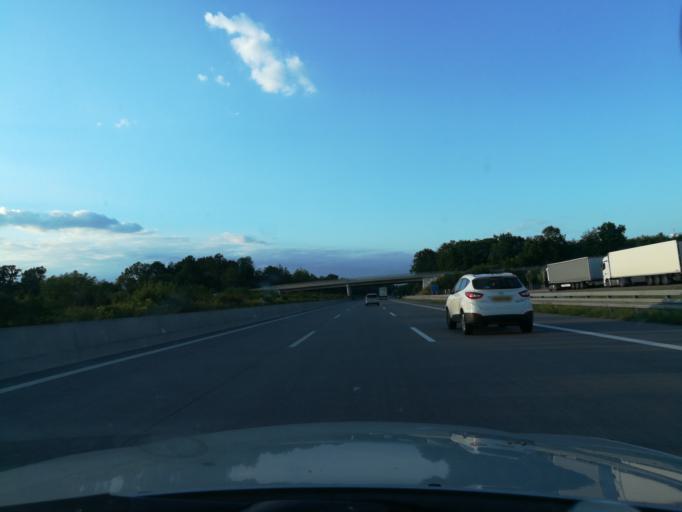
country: DE
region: Baden-Wuerttemberg
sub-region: Freiburg Region
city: Willstatt
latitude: 48.4993
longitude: 7.9042
